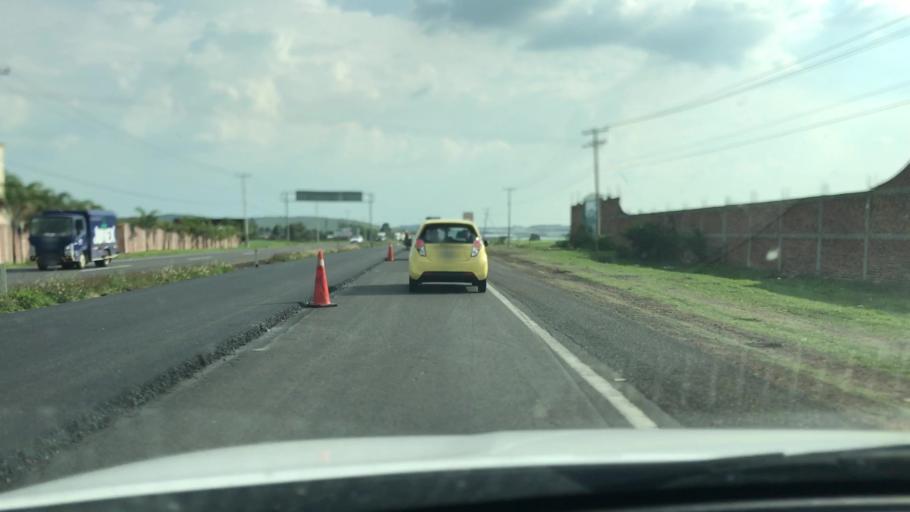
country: MX
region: Guanajuato
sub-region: Irapuato
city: Colonia Morelos de Guadalupe de Rivera
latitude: 20.5867
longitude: -101.4290
